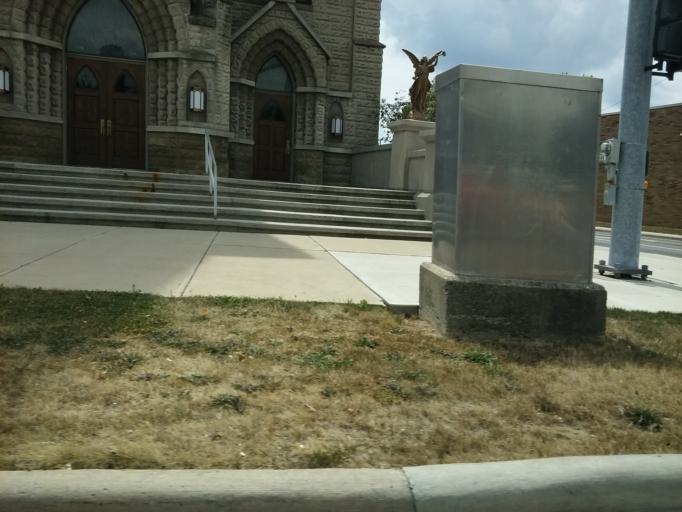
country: US
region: Ohio
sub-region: Hancock County
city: Findlay
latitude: 41.0398
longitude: -83.6597
